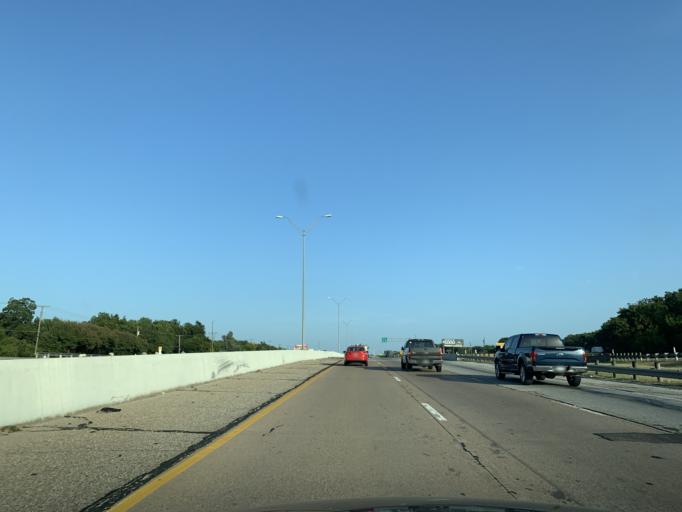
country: US
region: Texas
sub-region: Dallas County
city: Hutchins
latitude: 32.7237
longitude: -96.6993
